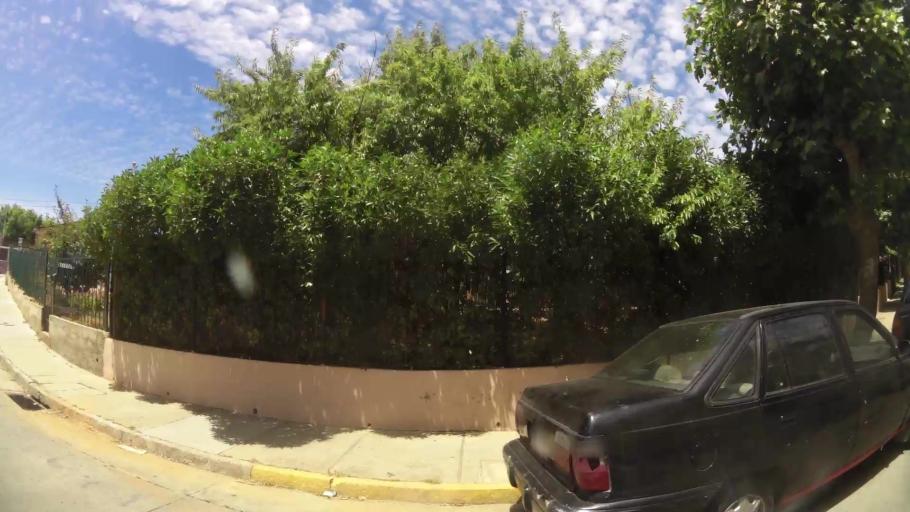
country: CL
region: Valparaiso
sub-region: Provincia de Valparaiso
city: Vina del Mar
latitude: -33.0473
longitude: -71.5763
